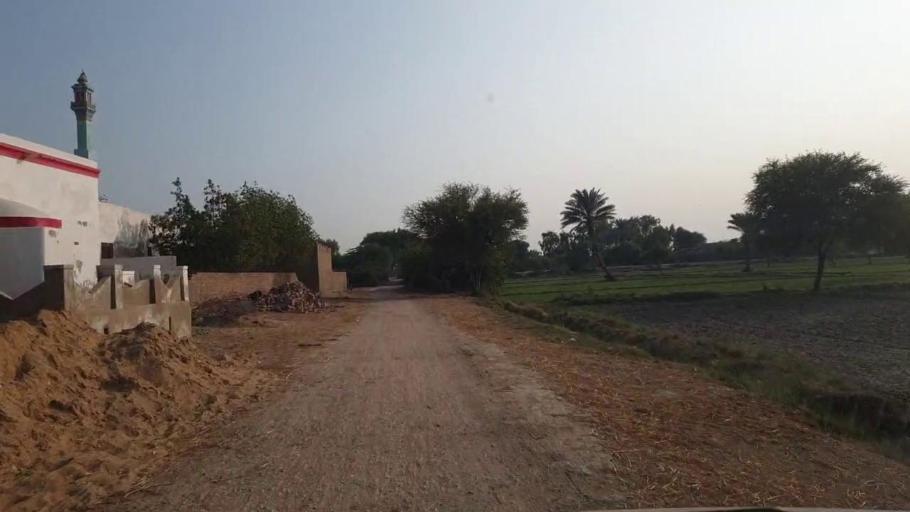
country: PK
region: Sindh
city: Rajo Khanani
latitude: 25.0332
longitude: 68.7771
